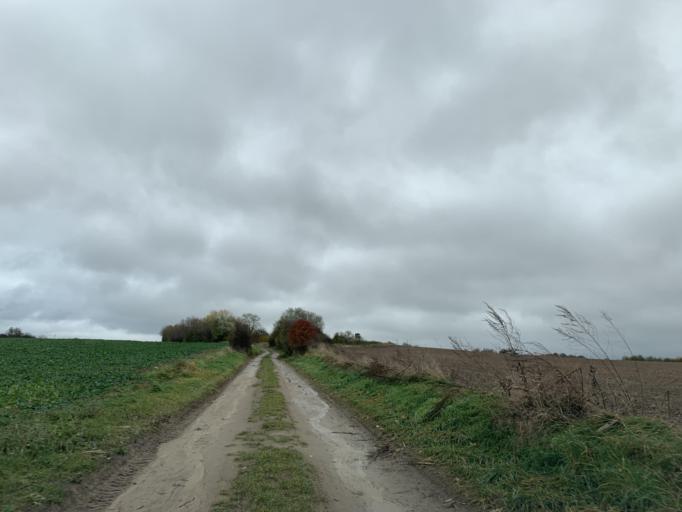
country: DE
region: Mecklenburg-Vorpommern
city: Blankensee
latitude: 53.3799
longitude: 13.2657
